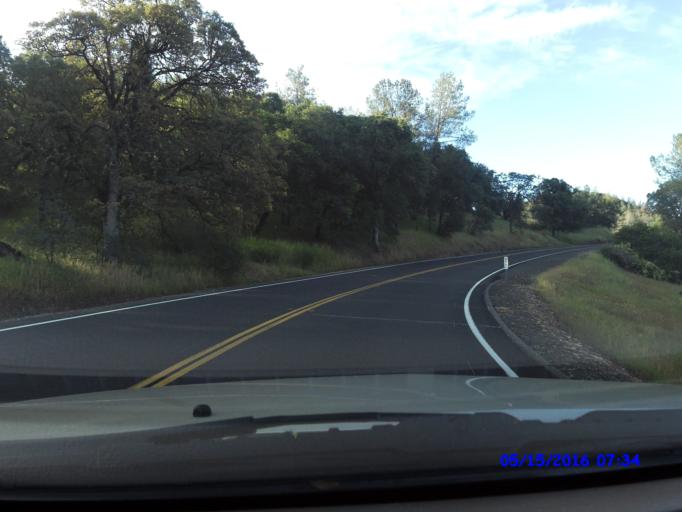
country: US
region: California
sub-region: Tuolumne County
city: Tuolumne City
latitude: 37.6878
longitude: -120.1770
